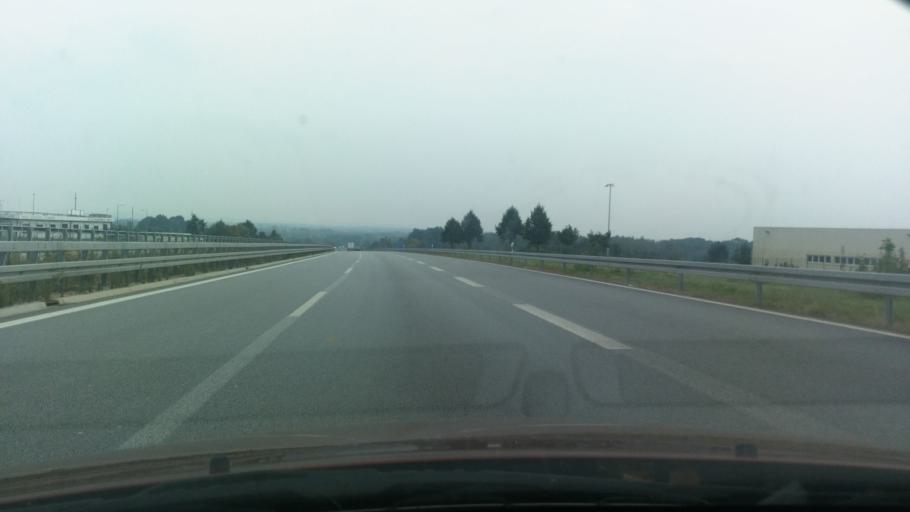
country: DE
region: Saxony
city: Goerlitz
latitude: 51.1866
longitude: 14.9894
